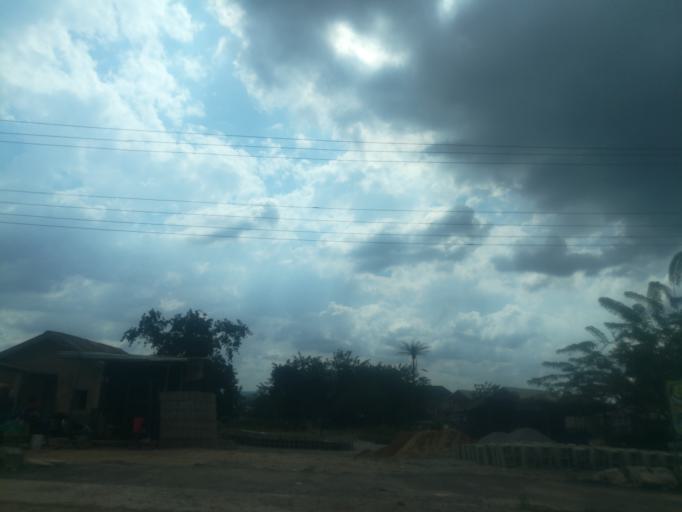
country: NG
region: Oyo
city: Ibadan
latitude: 7.4309
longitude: 3.8360
